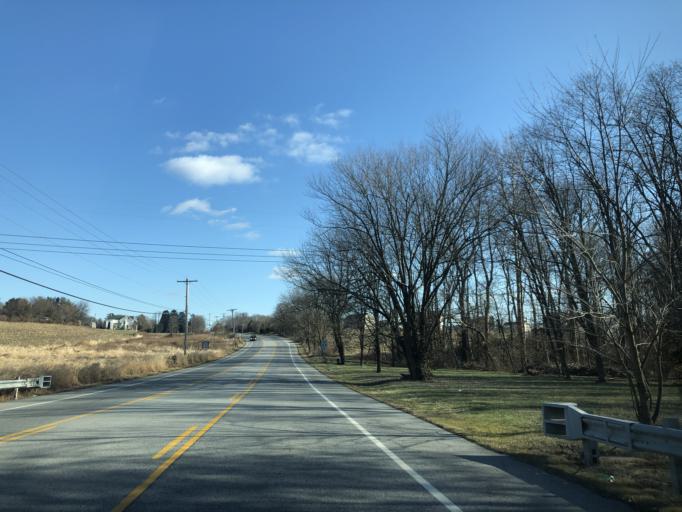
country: US
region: Pennsylvania
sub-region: Chester County
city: Parkesburg
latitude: 39.9815
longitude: -75.9088
